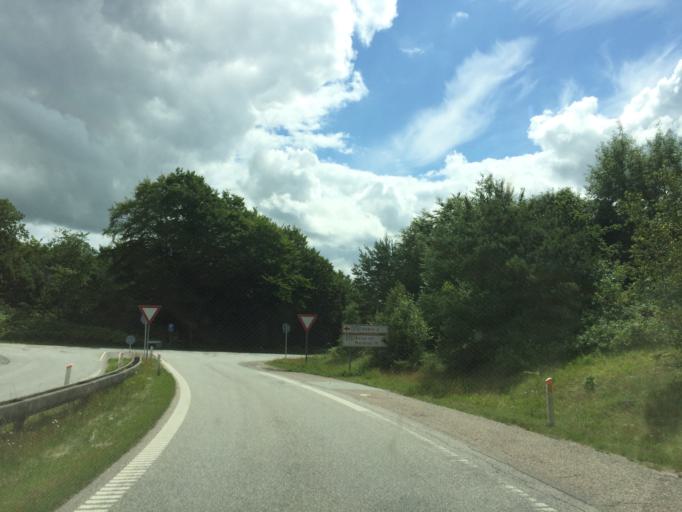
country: DK
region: North Denmark
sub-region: Mariagerfjord Kommune
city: Hobro
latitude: 56.6238
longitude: 9.7306
